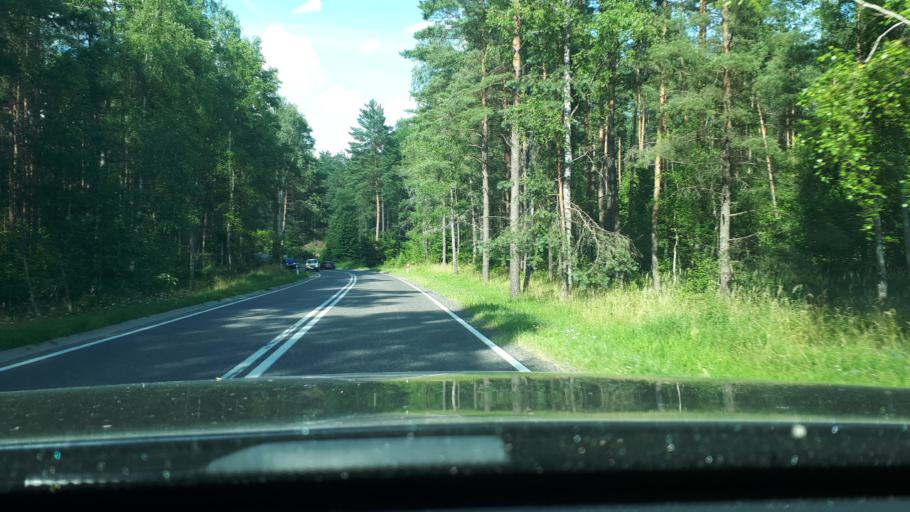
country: PL
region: Warmian-Masurian Voivodeship
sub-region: Powiat olsztynski
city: Stawiguda
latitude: 53.5312
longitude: 20.4589
